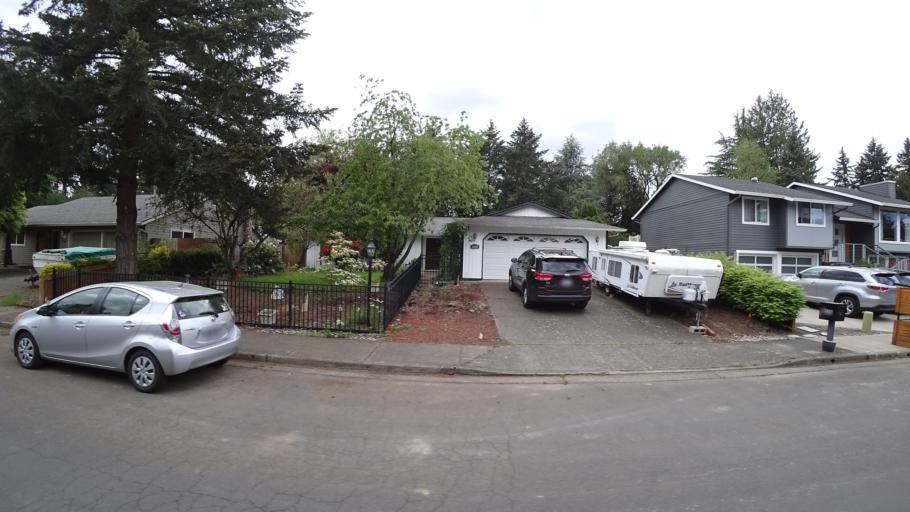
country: US
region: Oregon
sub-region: Washington County
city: Beaverton
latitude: 45.4803
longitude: -122.8349
